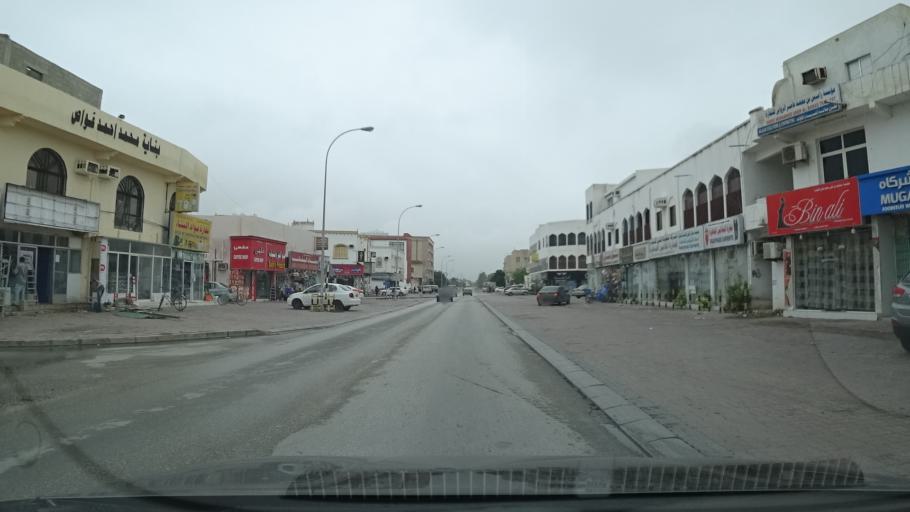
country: OM
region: Zufar
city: Salalah
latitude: 17.0097
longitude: 54.0732
